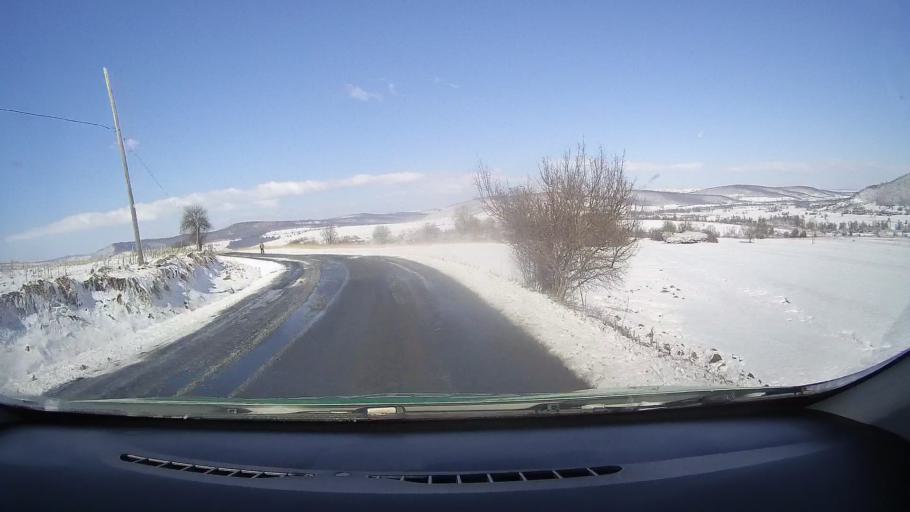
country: RO
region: Sibiu
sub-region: Comuna Rosia
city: Rosia
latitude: 45.7995
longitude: 24.3854
